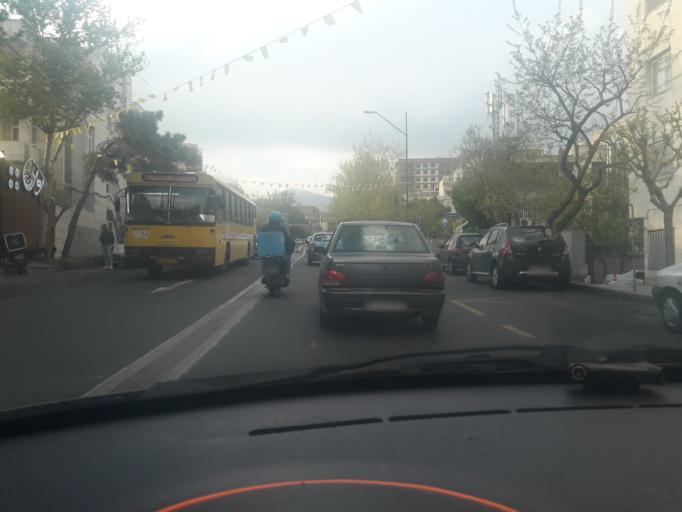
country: IR
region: Tehran
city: Tehran
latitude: 35.7454
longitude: 51.4049
